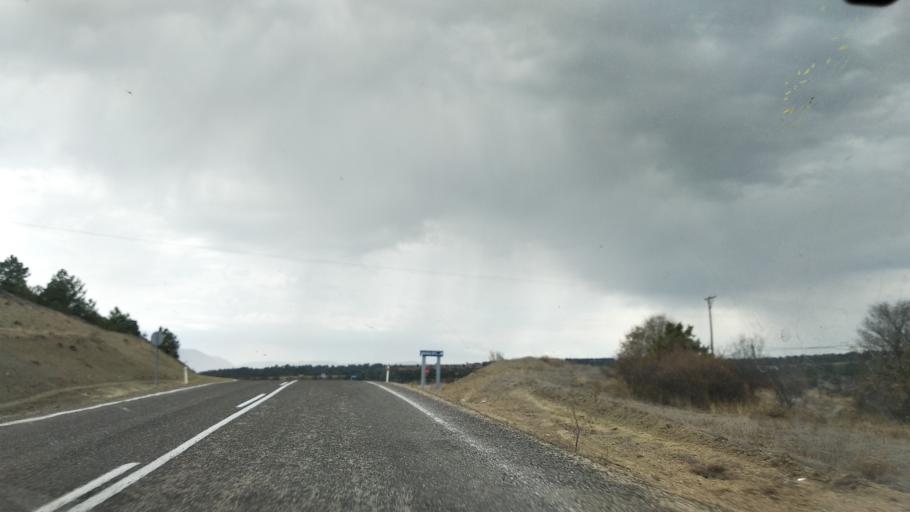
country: TR
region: Bolu
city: Seben
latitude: 40.3507
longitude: 31.4774
